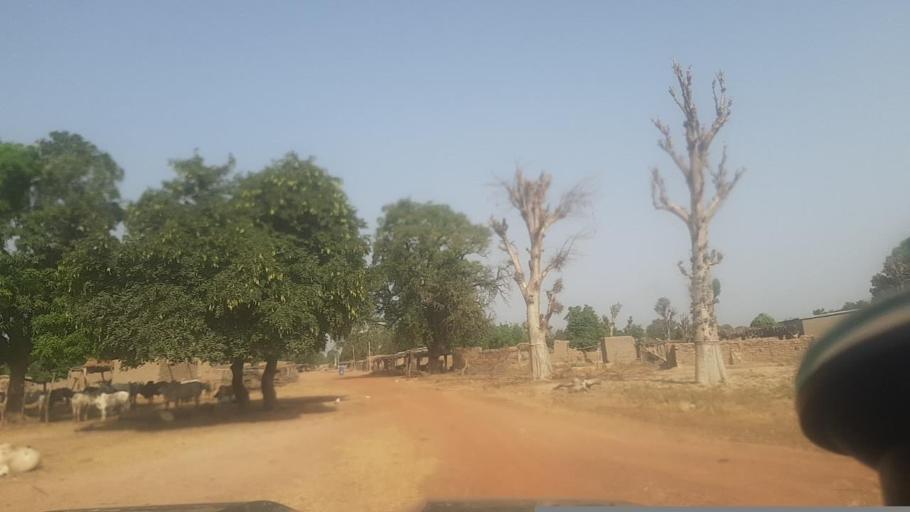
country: ML
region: Segou
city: Bla
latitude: 12.8464
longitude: -5.9930
